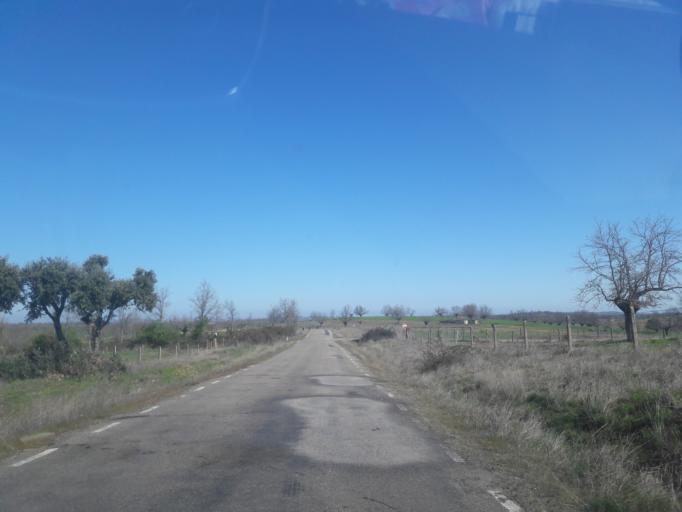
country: ES
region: Castille and Leon
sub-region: Provincia de Salamanca
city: Valsalabroso
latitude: 41.1361
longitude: -6.4829
